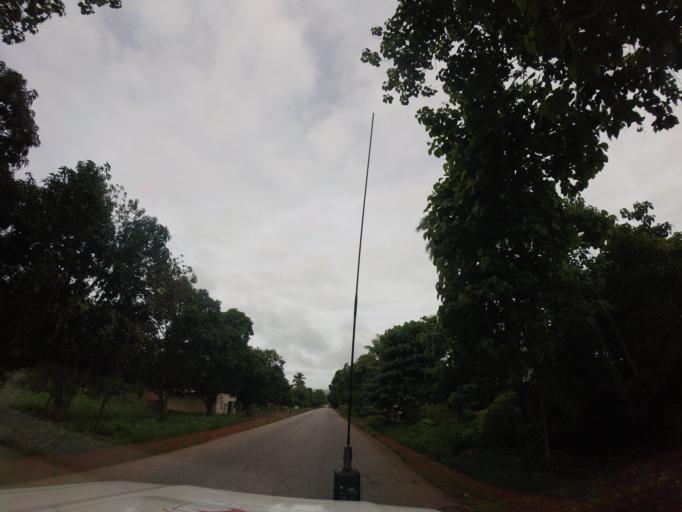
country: GN
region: Kindia
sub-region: Kindia
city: Kindia
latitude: 9.9492
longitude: -12.9535
